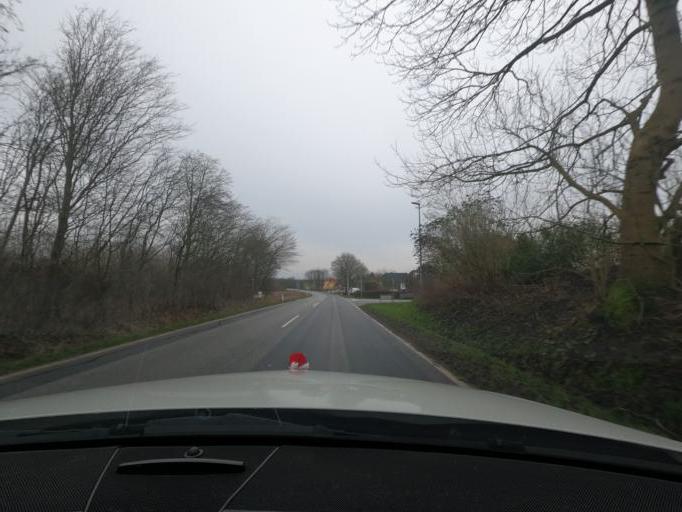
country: DK
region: South Denmark
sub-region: Haderslev Kommune
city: Starup
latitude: 55.1940
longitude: 9.5201
